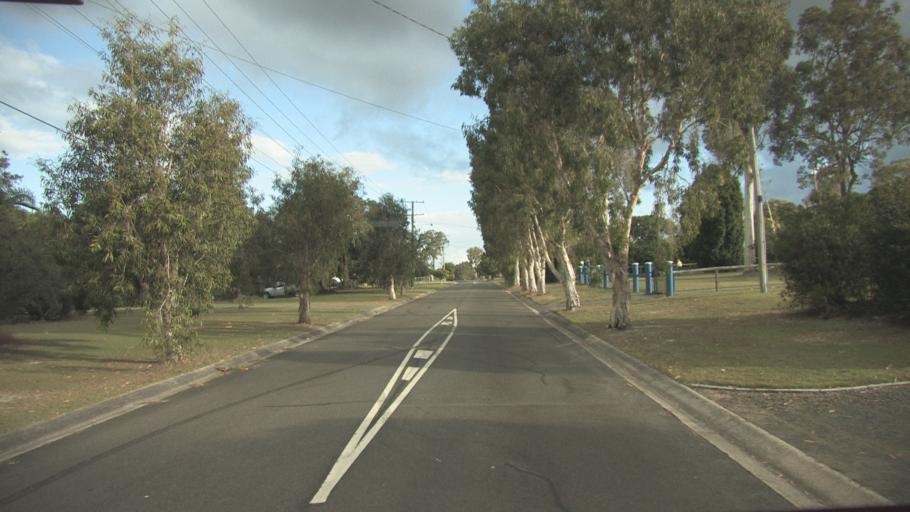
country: AU
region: Queensland
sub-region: Logan
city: Park Ridge South
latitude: -27.7060
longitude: 153.0203
